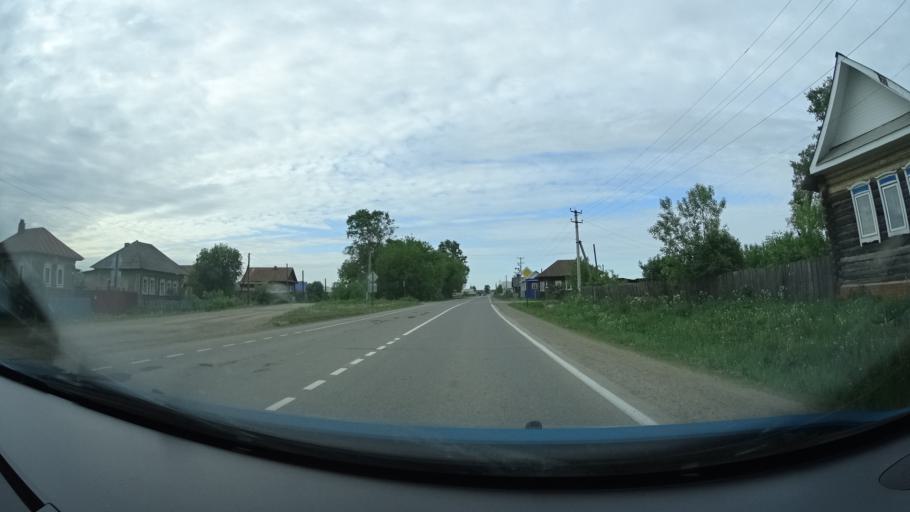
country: RU
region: Perm
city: Barda
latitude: 56.8896
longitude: 55.6028
